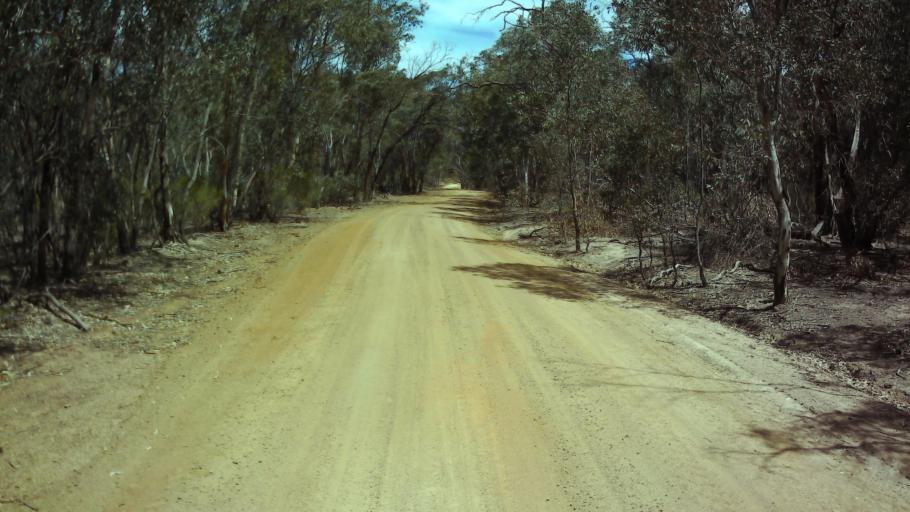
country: AU
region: New South Wales
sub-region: Weddin
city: Grenfell
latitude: -33.8025
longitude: 148.1600
